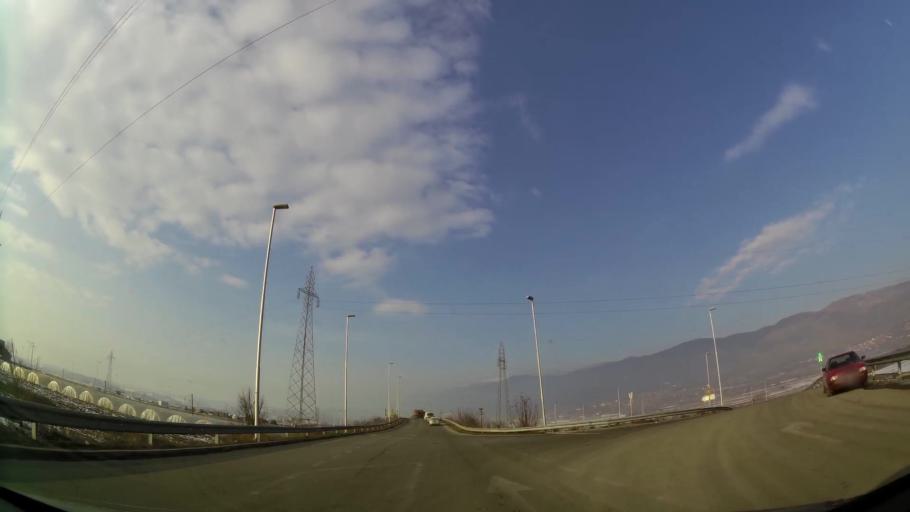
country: MK
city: Creshevo
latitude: 42.0306
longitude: 21.5121
